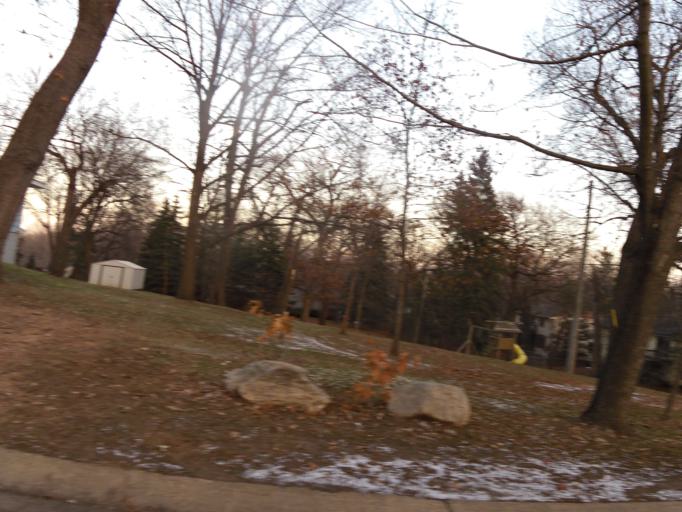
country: US
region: Minnesota
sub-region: Scott County
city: Prior Lake
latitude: 44.7094
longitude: -93.4421
